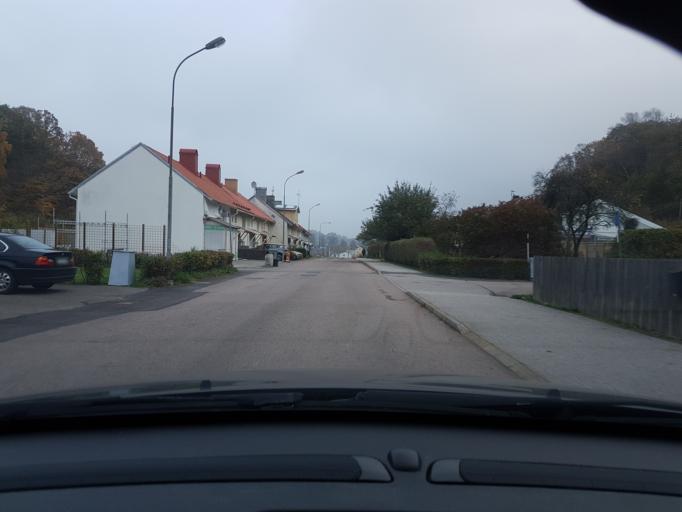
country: SE
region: Vaestra Goetaland
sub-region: Ale Kommun
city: Surte
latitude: 57.8262
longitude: 12.0211
